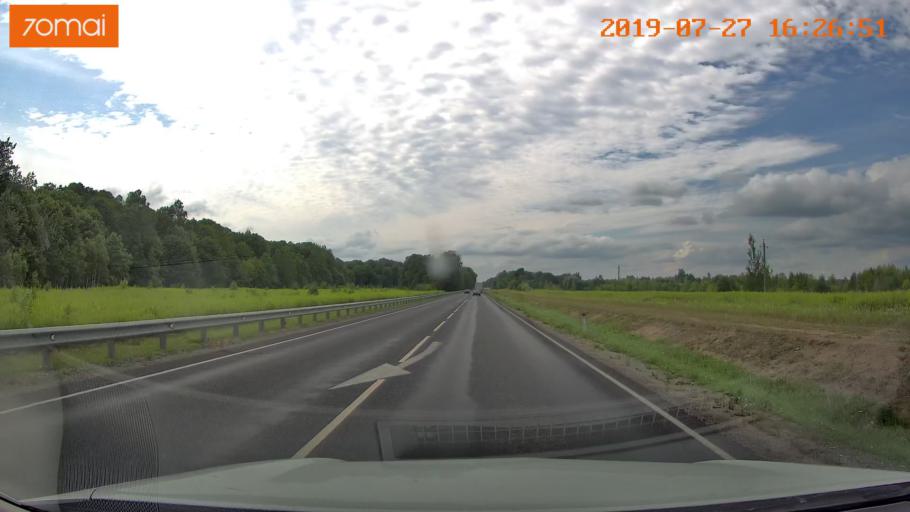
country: RU
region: Kaliningrad
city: Zheleznodorozhnyy
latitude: 54.6417
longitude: 21.4012
